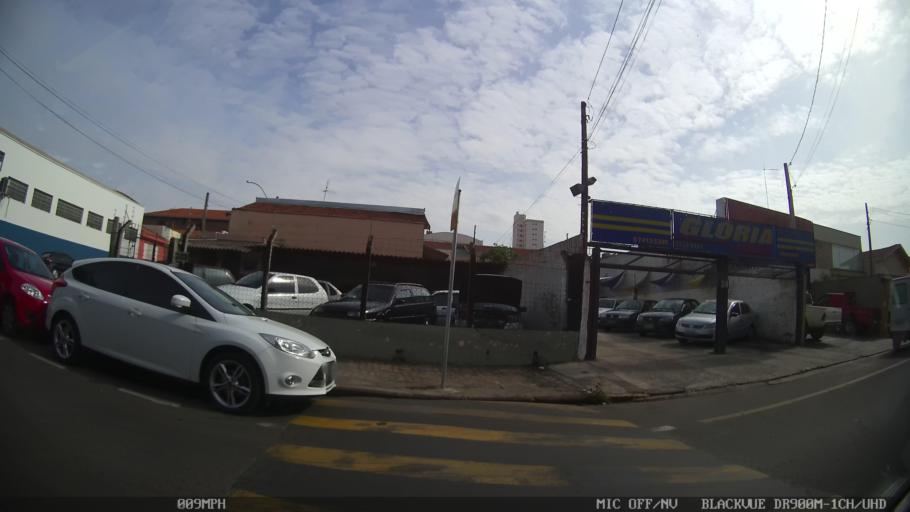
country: BR
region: Sao Paulo
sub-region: Piracicaba
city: Piracicaba
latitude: -22.7388
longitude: -47.6522
